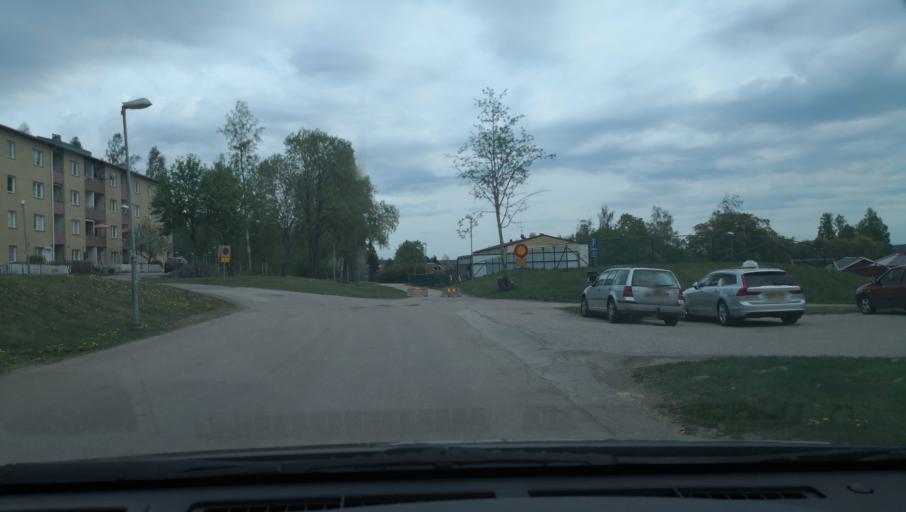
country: SE
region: Vaestmanland
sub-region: Skinnskattebergs Kommun
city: Skinnskatteberg
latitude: 59.8289
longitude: 15.6969
